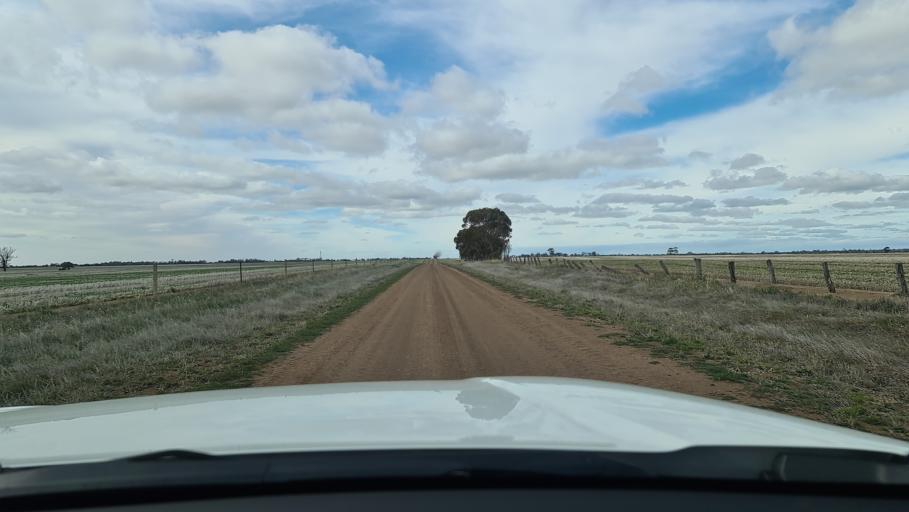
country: AU
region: Victoria
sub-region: Horsham
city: Horsham
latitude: -36.6313
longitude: 142.4279
